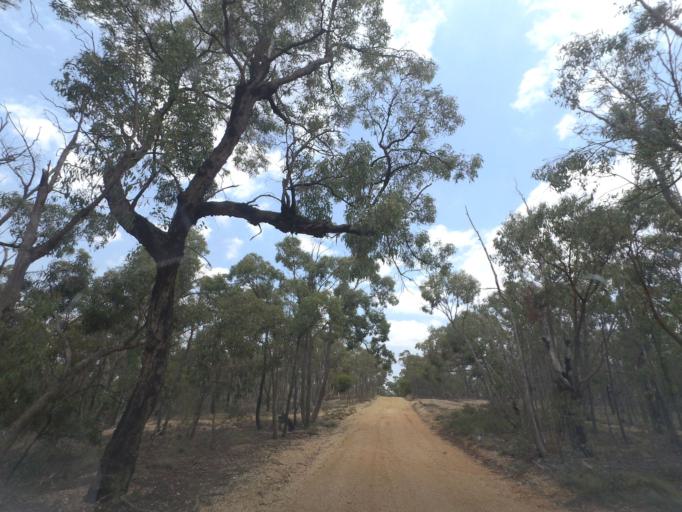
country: AU
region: Victoria
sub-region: Moorabool
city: Bacchus Marsh
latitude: -37.5828
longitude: 144.4416
